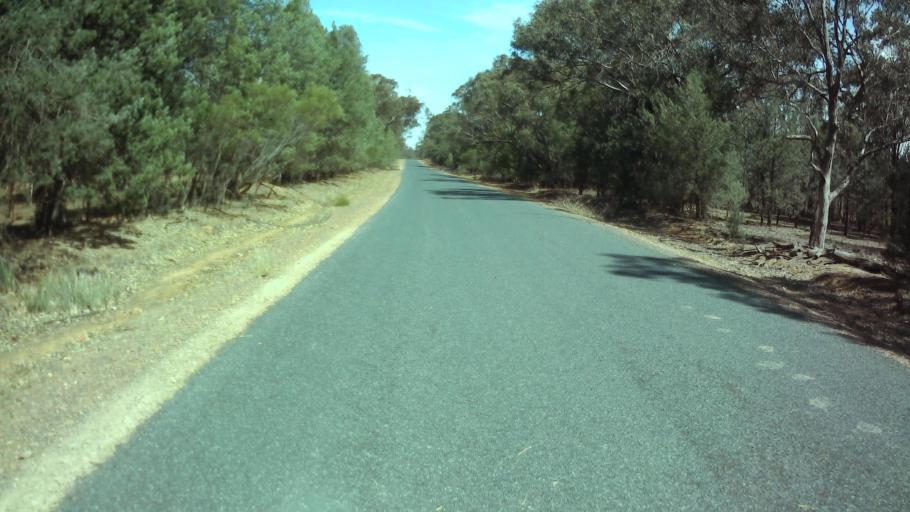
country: AU
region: New South Wales
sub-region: Weddin
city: Grenfell
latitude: -34.0707
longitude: 148.1398
